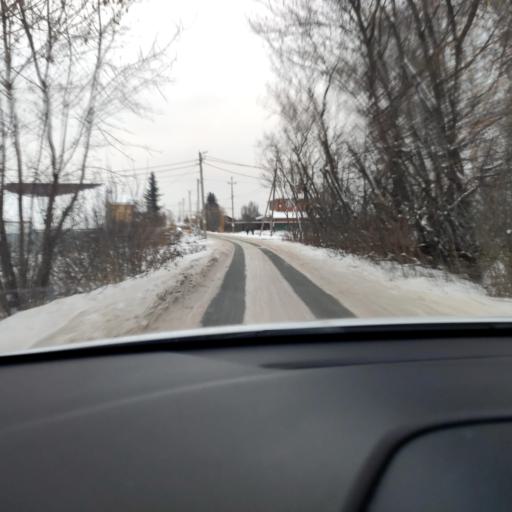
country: RU
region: Tatarstan
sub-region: Gorod Kazan'
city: Kazan
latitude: 55.8750
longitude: 49.1497
